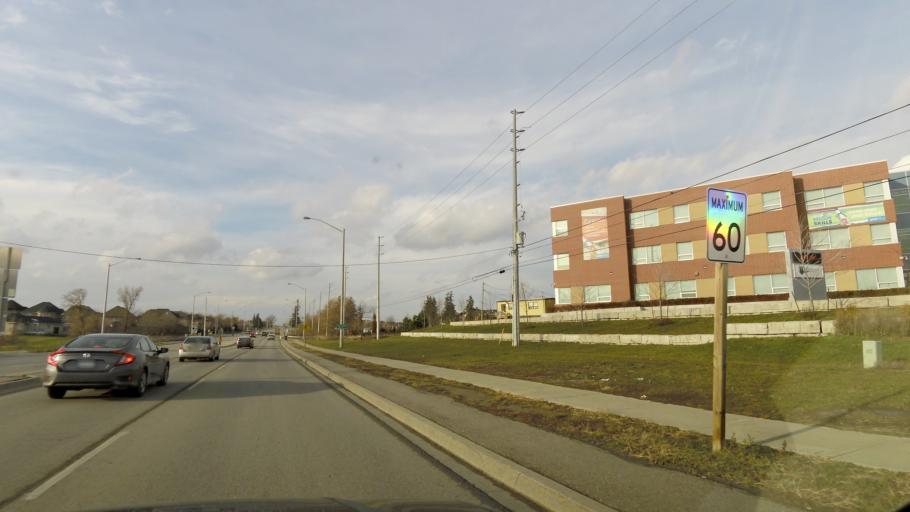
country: CA
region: Ontario
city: Brampton
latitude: 43.7832
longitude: -79.6779
